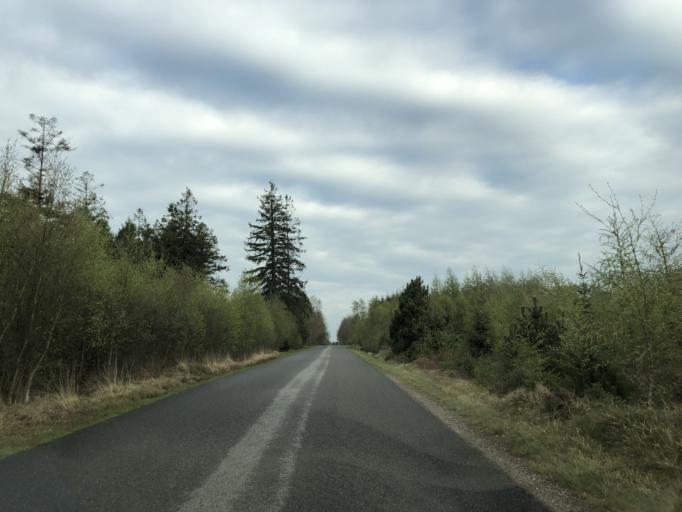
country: DK
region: Central Jutland
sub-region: Holstebro Kommune
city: Holstebro
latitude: 56.3177
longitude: 8.5177
